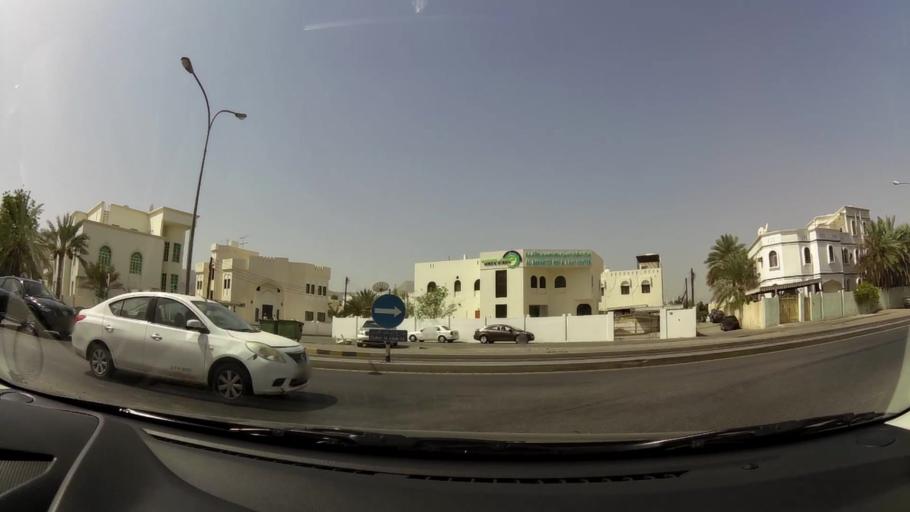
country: OM
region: Muhafazat Masqat
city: Bawshar
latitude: 23.5932
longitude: 58.4239
